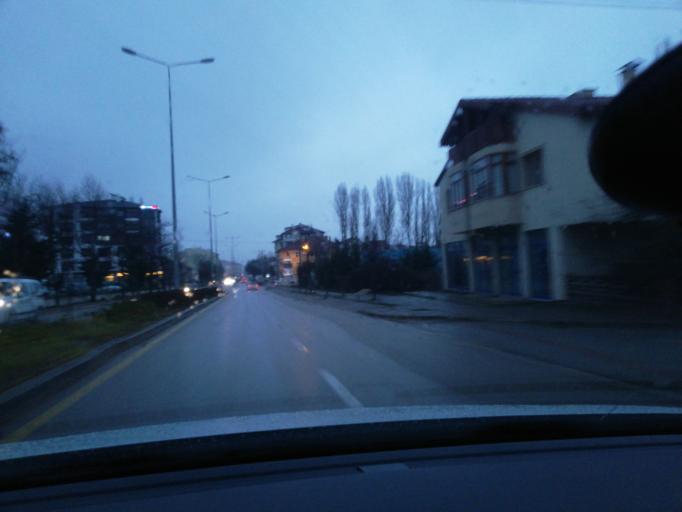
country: TR
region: Bolu
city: Bolu
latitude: 40.7301
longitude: 31.5839
